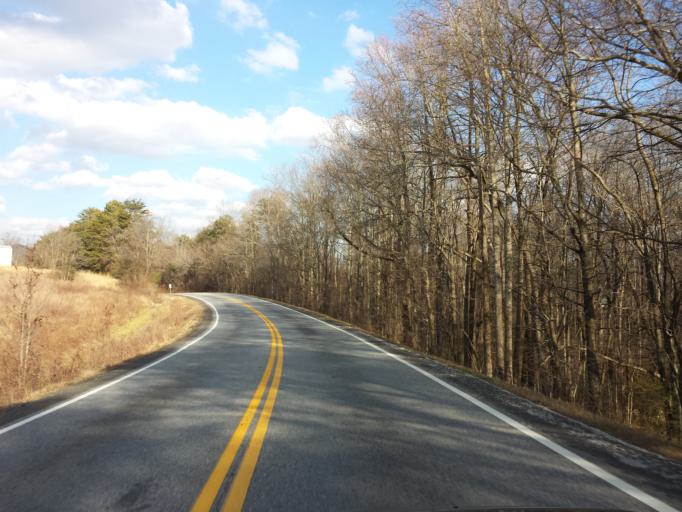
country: US
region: Georgia
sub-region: White County
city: Cleveland
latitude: 34.5359
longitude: -83.8137
